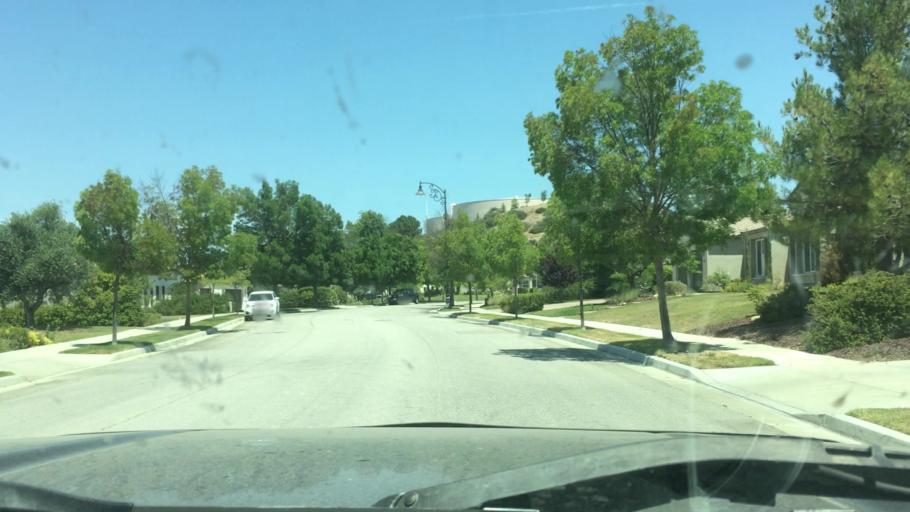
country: US
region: California
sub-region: San Luis Obispo County
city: Paso Robles
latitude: 35.6267
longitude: -120.6601
